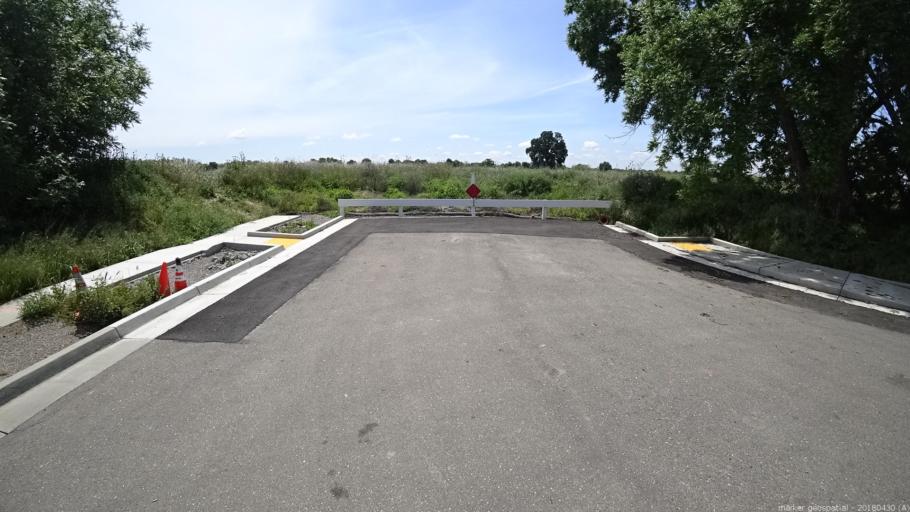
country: US
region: California
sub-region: Yolo County
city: West Sacramento
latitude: 38.5404
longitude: -121.5308
